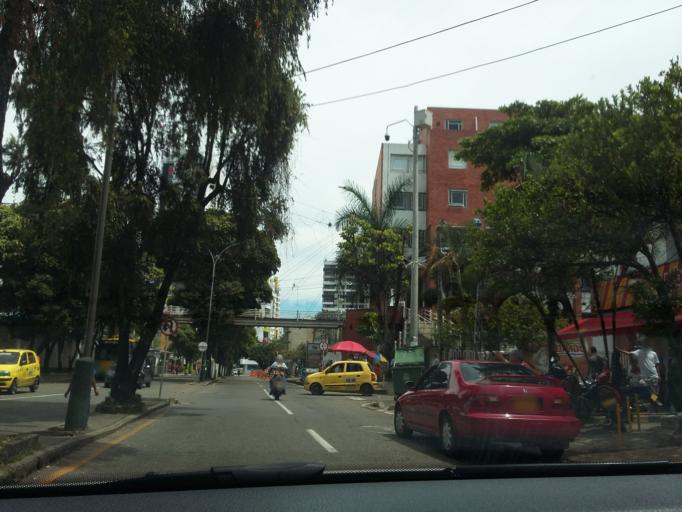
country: CO
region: Santander
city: Bucaramanga
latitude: 7.1284
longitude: -73.1135
